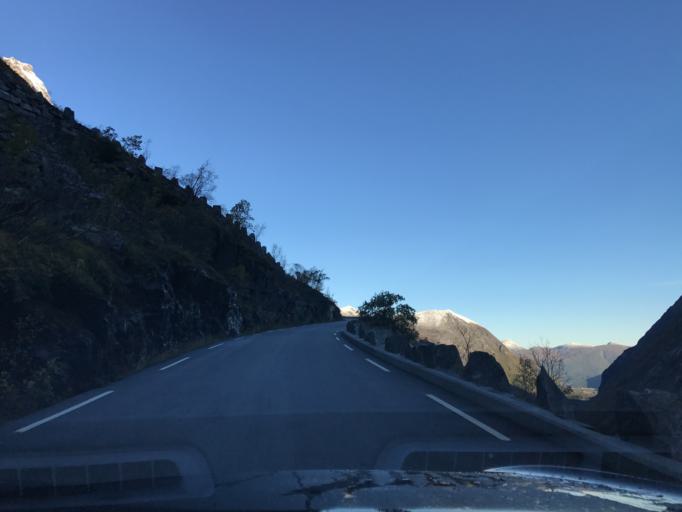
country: NO
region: More og Romsdal
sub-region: Rauma
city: Andalsnes
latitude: 62.4588
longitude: 7.6712
